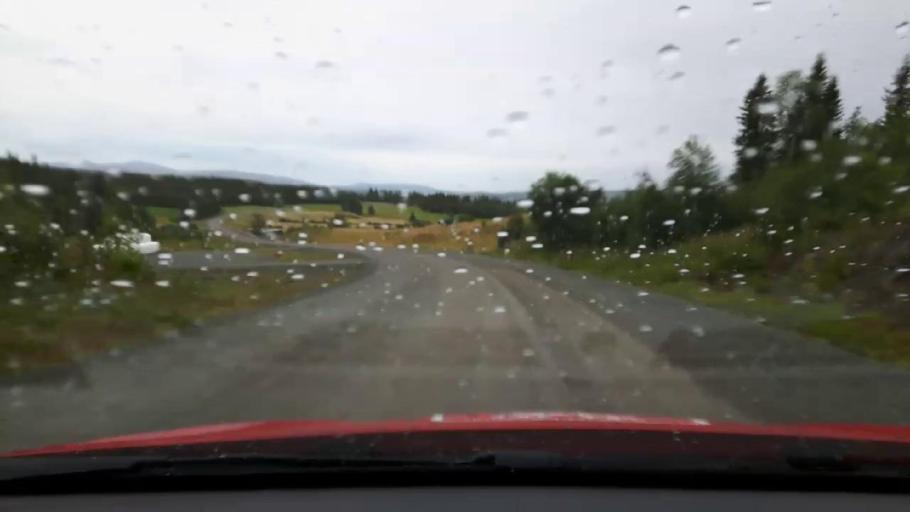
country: SE
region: Jaemtland
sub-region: Are Kommun
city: Are
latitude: 63.4734
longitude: 12.5633
